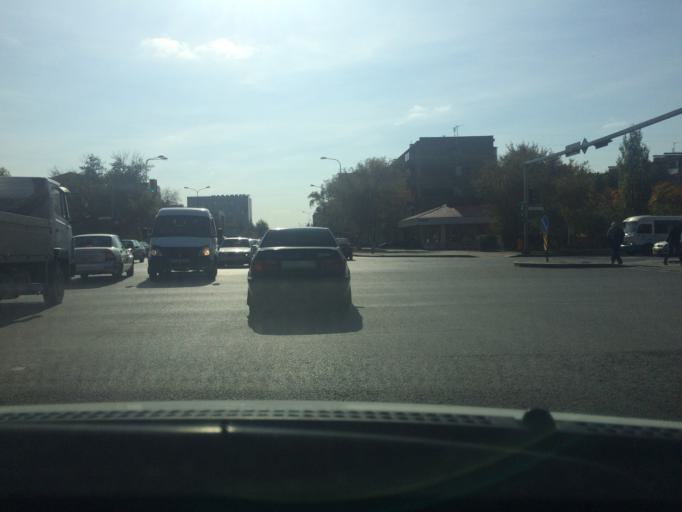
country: KZ
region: Astana Qalasy
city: Astana
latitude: 51.1775
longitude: 71.4239
